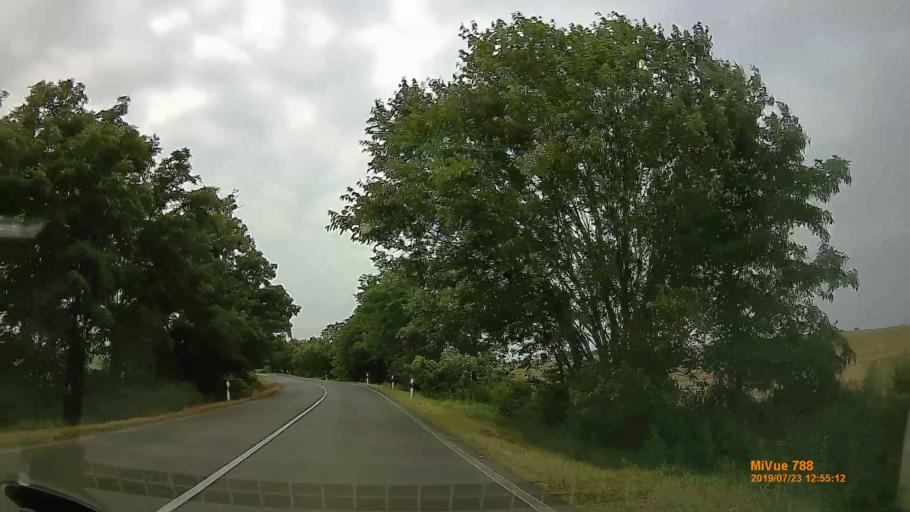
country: HU
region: Szabolcs-Szatmar-Bereg
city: Nagycserkesz
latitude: 47.9604
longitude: 21.5232
